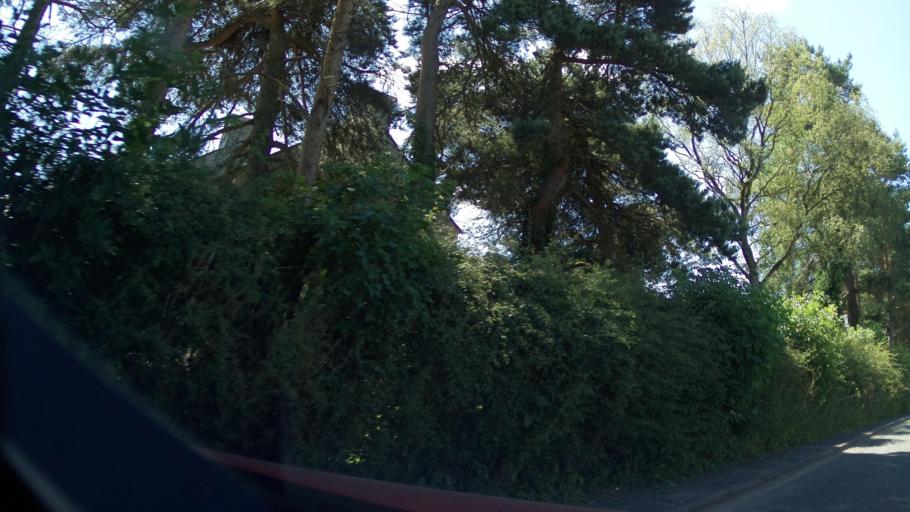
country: GB
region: England
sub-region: Derbyshire
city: Bakewell
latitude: 53.2095
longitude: -1.6866
